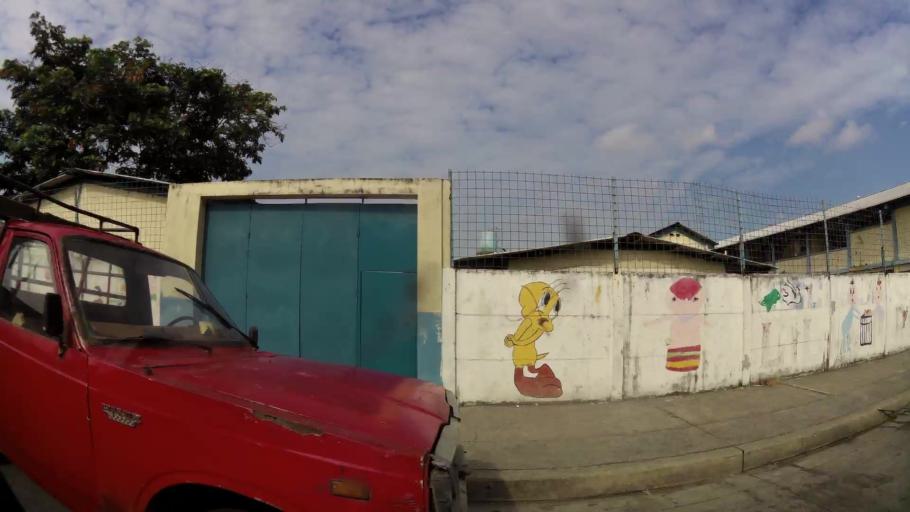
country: EC
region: Guayas
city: Guayaquil
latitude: -2.2562
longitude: -79.8733
